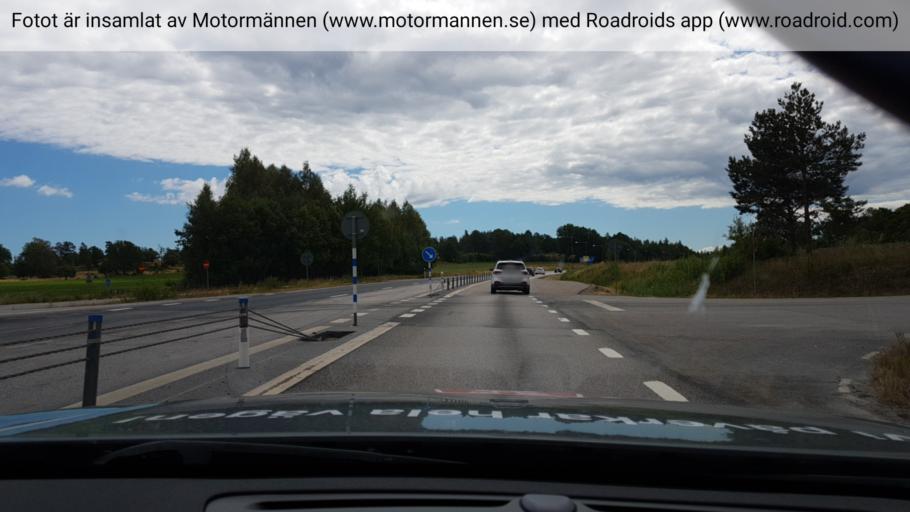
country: SE
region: Kalmar
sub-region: Vasterviks Kommun
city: Vaestervik
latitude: 57.7709
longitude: 16.5545
